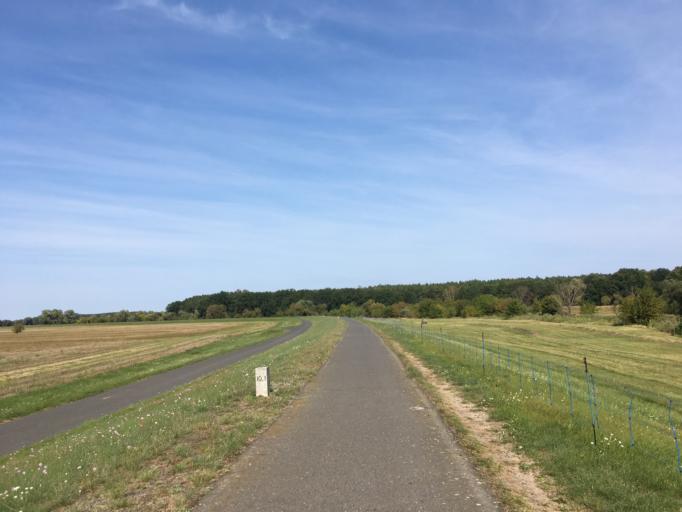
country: PL
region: Lubusz
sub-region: Powiat krosnienski
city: Gubin
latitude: 52.0397
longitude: 14.7482
